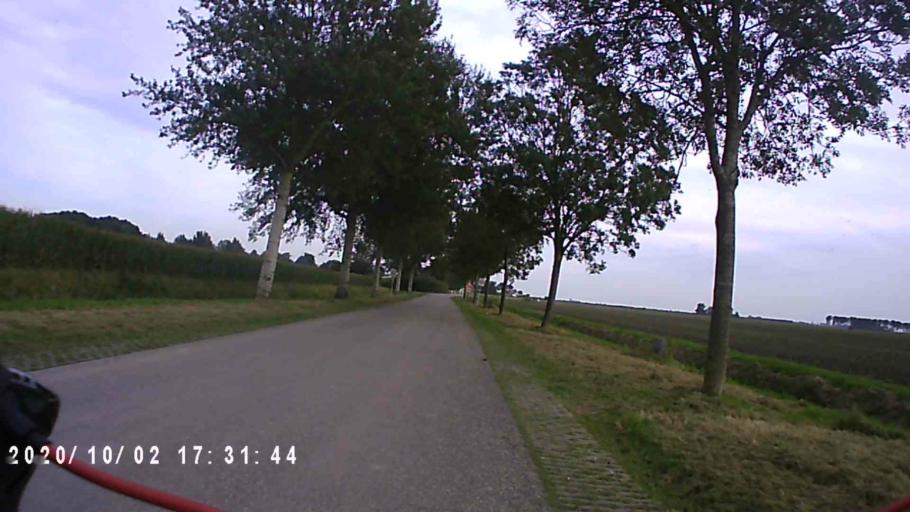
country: NL
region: Groningen
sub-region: Gemeente De Marne
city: Ulrum
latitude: 53.3361
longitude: 6.3336
